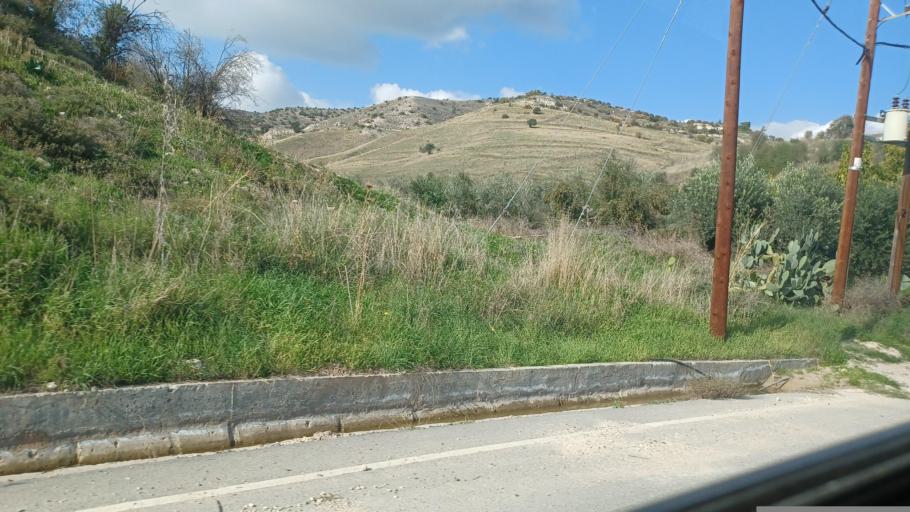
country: CY
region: Pafos
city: Mesogi
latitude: 34.7793
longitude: 32.5813
